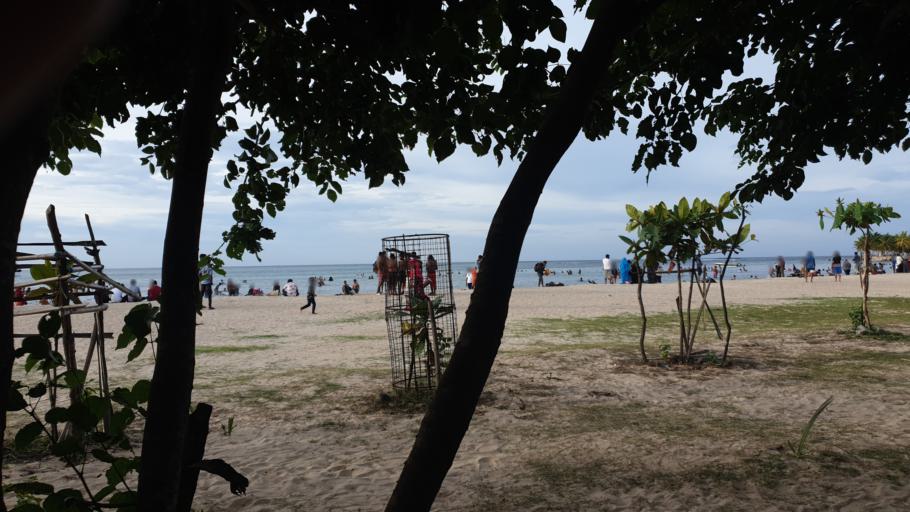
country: LK
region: Eastern Province
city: Eravur Town
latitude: 7.9249
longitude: 81.5667
